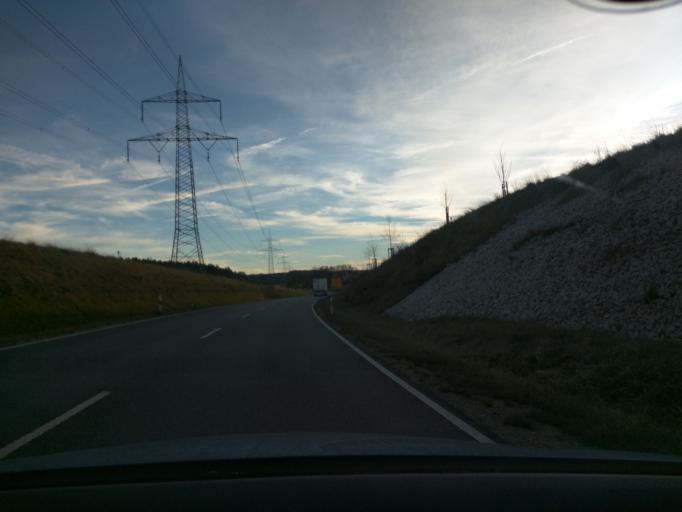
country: DE
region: Bavaria
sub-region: Upper Bavaria
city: Au in der Hallertau
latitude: 48.5542
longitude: 11.7286
